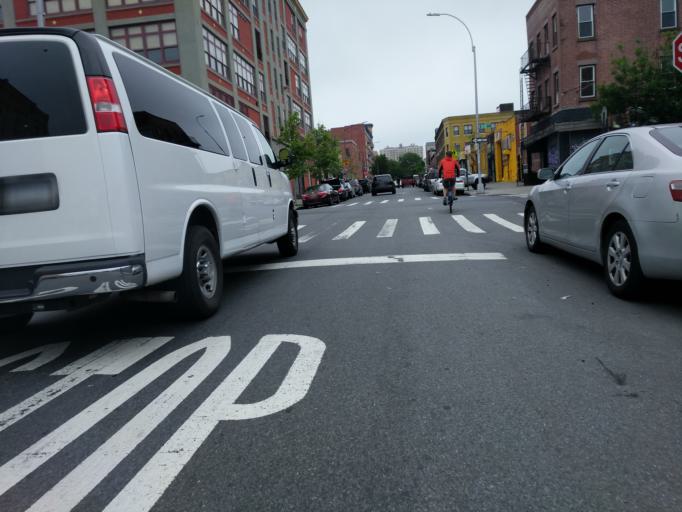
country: US
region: New York
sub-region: Kings County
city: Brooklyn
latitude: 40.6792
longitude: -73.9619
